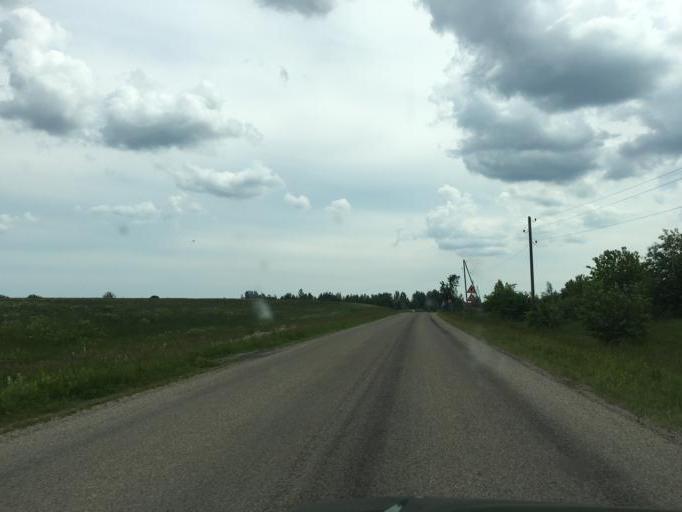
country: LV
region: Rugaju
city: Rugaji
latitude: 56.8495
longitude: 27.0899
